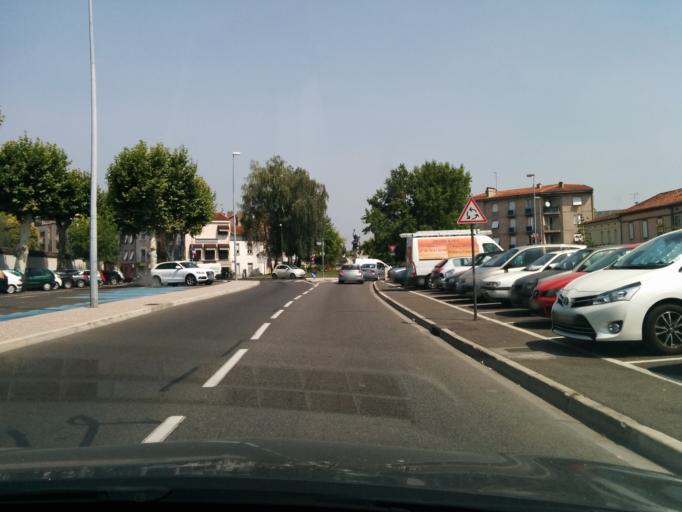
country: FR
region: Midi-Pyrenees
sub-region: Departement du Tarn
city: Albi
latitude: 43.9214
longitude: 2.1495
